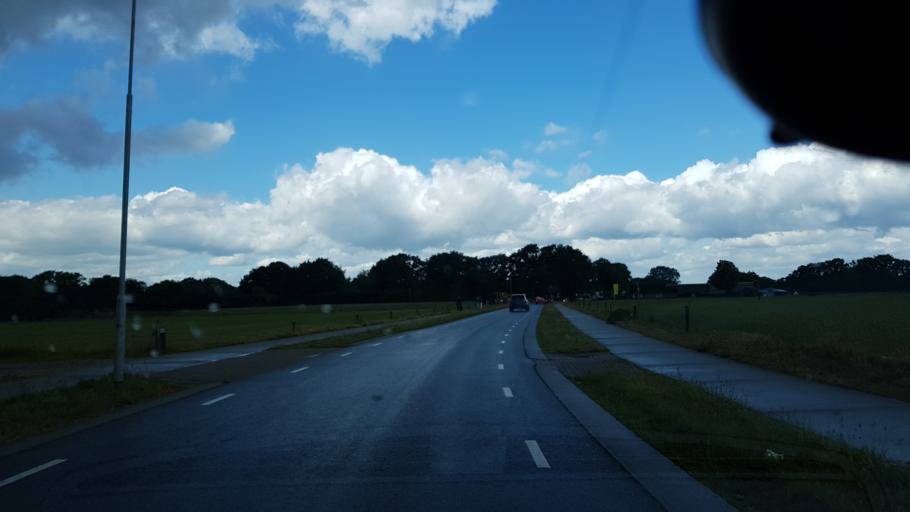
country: NL
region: Gelderland
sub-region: Gemeente Ermelo
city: Horst
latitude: 52.2968
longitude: 5.5931
